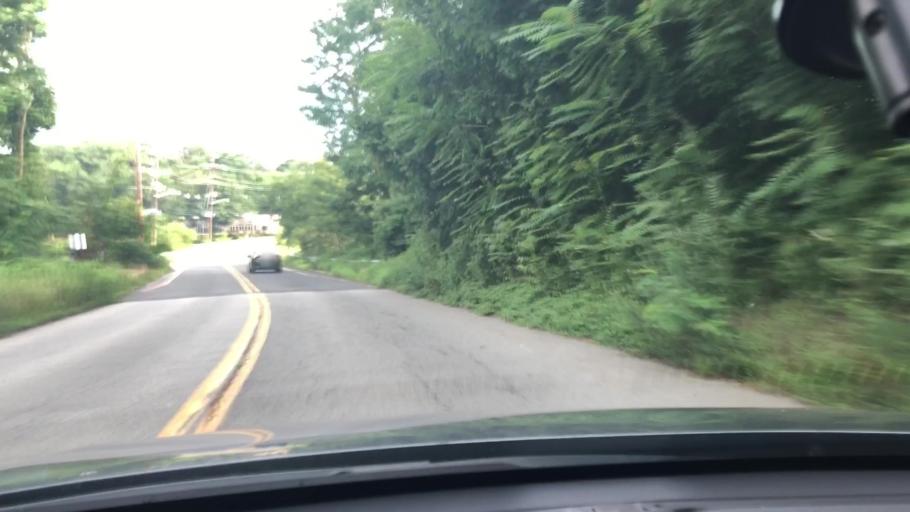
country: US
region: New Jersey
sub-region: Middlesex County
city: Milltown
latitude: 40.4387
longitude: -74.4655
